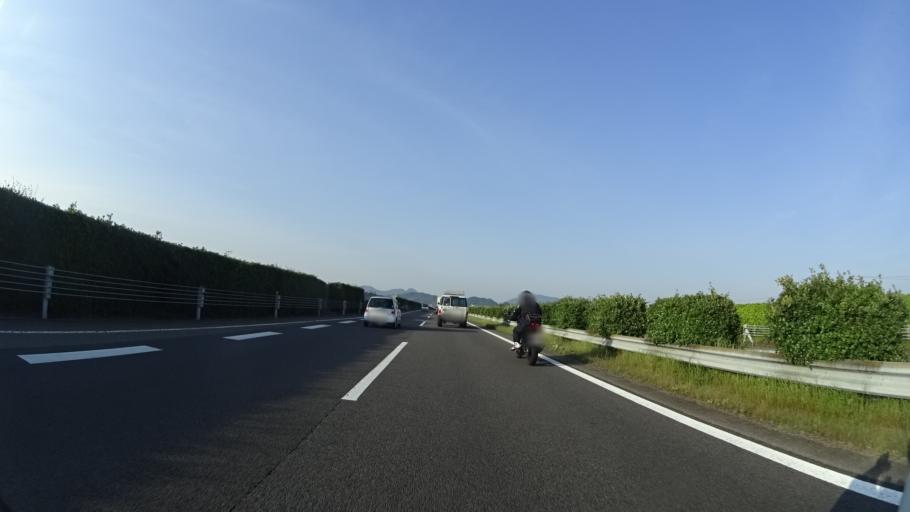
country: JP
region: Kagawa
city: Kan'onjicho
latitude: 34.1179
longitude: 133.6891
